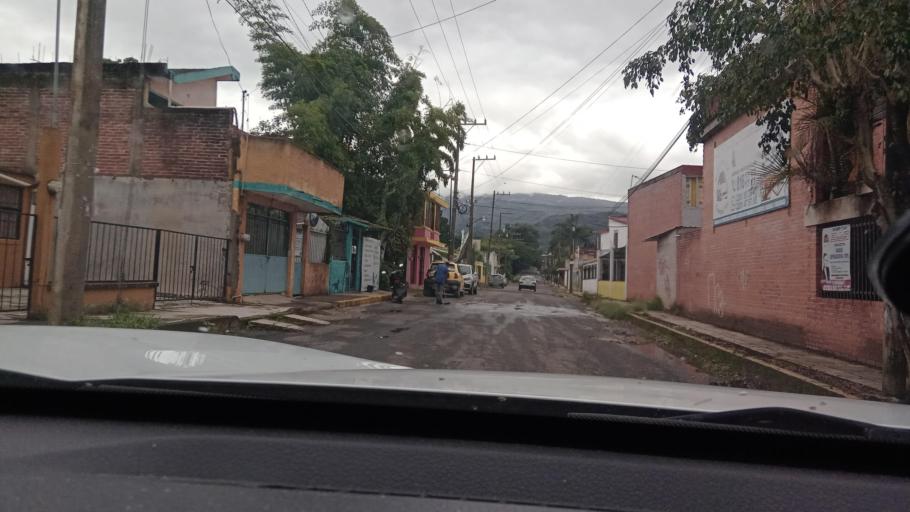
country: MX
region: Veracruz
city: Coatepec
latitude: 19.4496
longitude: -96.9721
